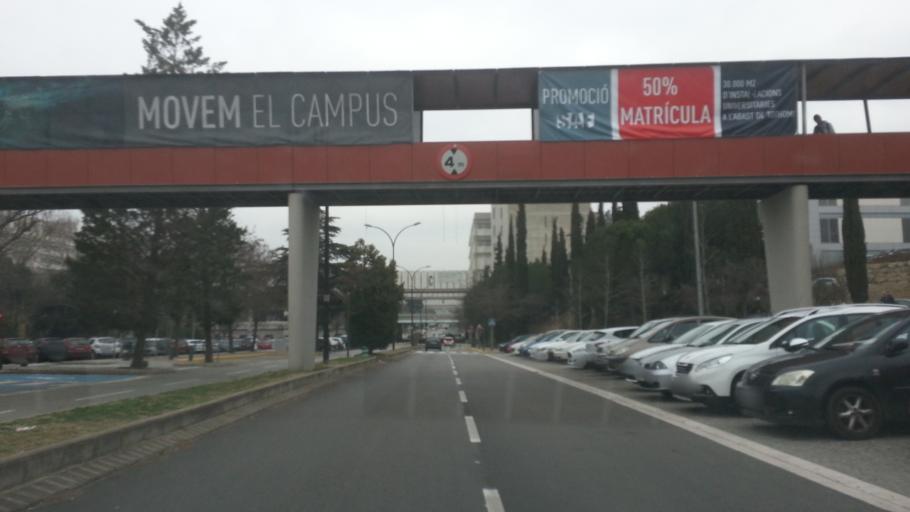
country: ES
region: Catalonia
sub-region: Provincia de Barcelona
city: Barbera del Valles
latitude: 41.4999
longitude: 2.1091
